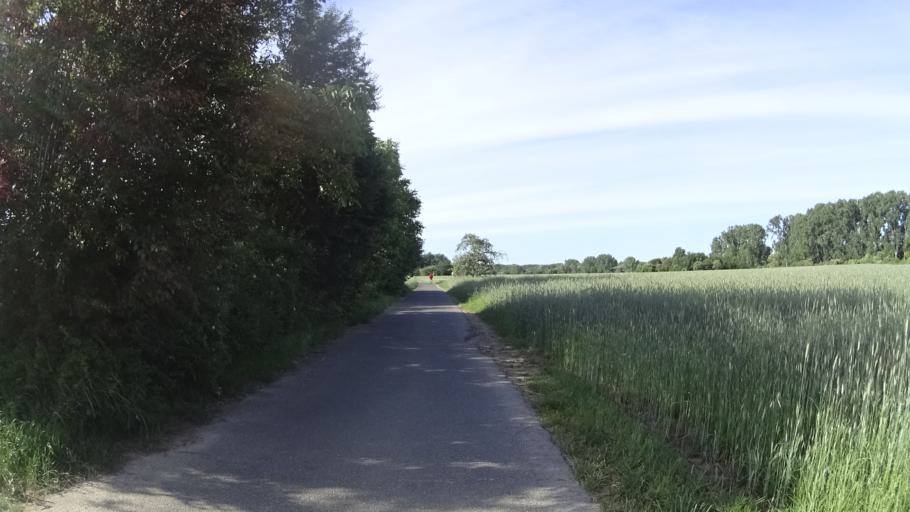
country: DE
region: Bavaria
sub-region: Regierungsbezirk Unterfranken
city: Kleinostheim
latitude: 50.0324
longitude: 9.0351
